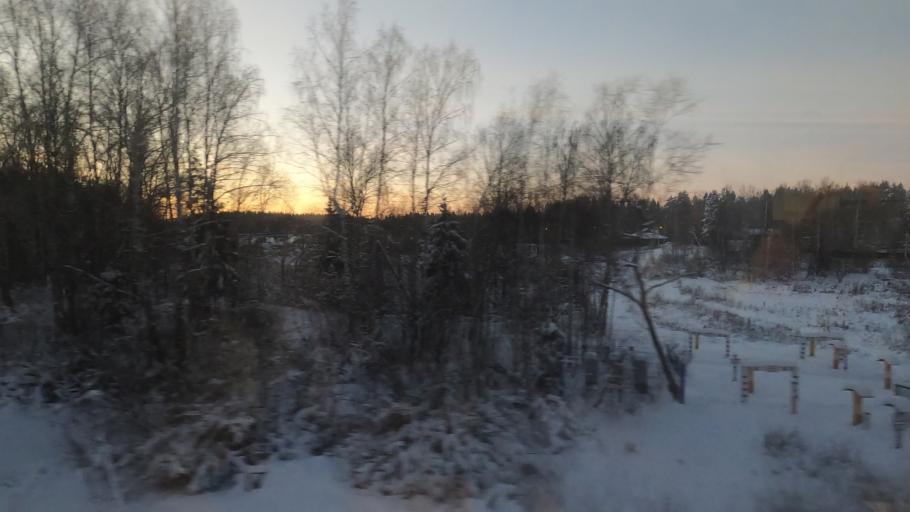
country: RU
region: Moskovskaya
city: Lugovaya
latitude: 56.0695
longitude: 37.4941
